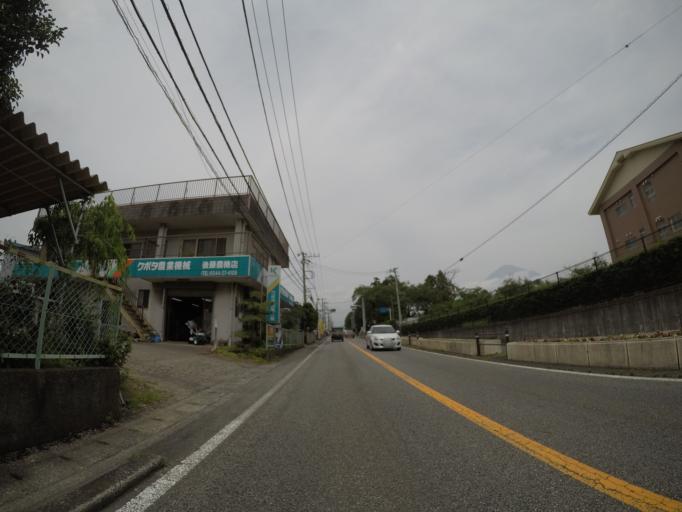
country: JP
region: Shizuoka
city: Fujinomiya
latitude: 35.2367
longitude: 138.6094
